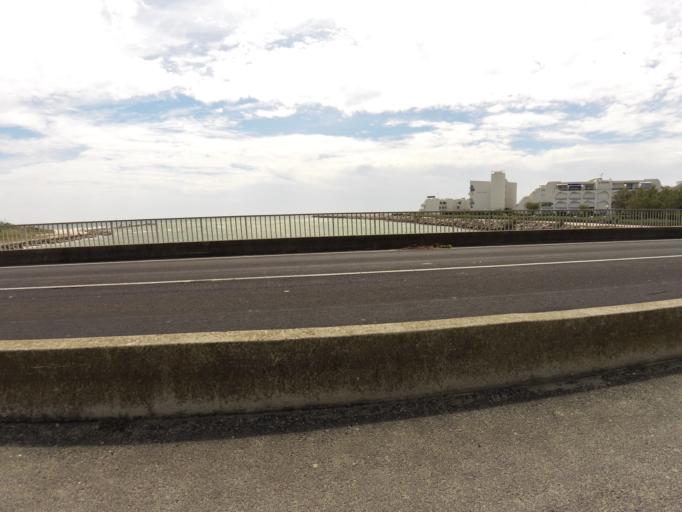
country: FR
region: Languedoc-Roussillon
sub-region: Departement de l'Herault
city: La Grande-Motte
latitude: 43.5563
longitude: 4.1015
